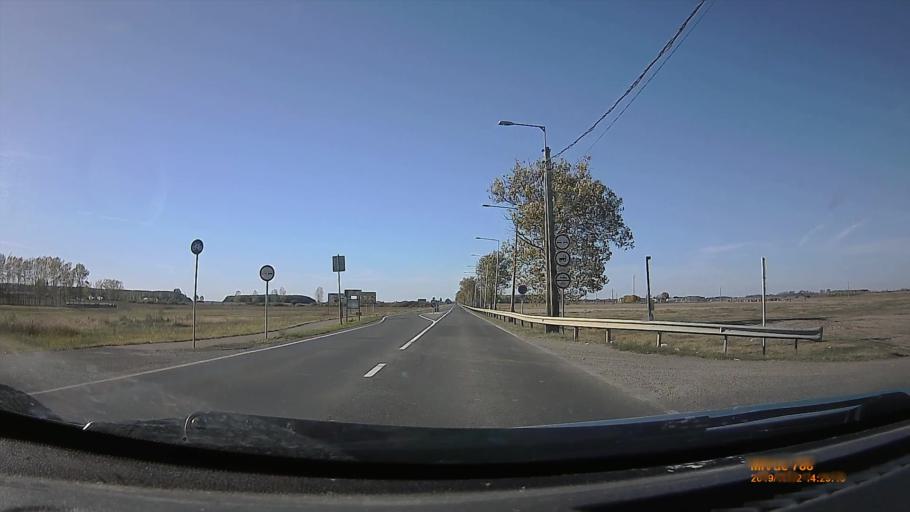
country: HU
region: Hajdu-Bihar
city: Berettyoujfalu
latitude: 47.1690
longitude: 21.6166
